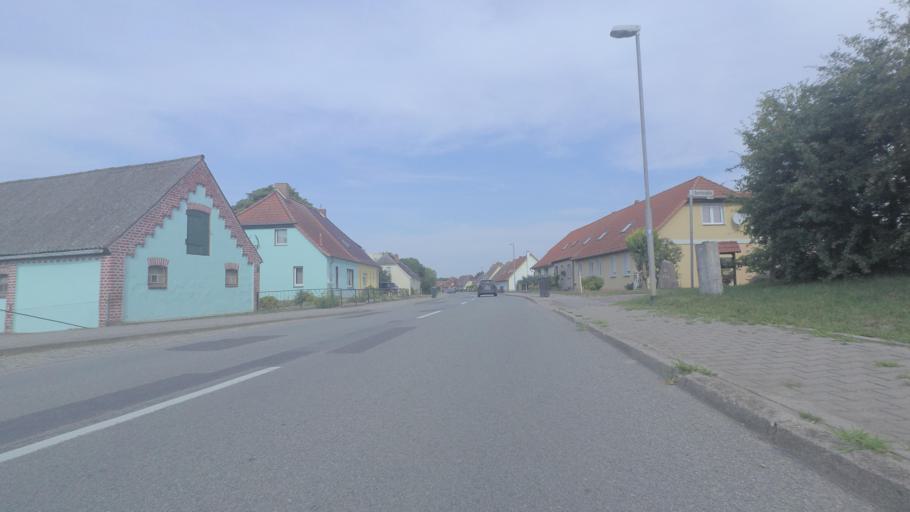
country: DE
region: Mecklenburg-Vorpommern
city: Gielow
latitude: 53.6486
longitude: 12.8296
